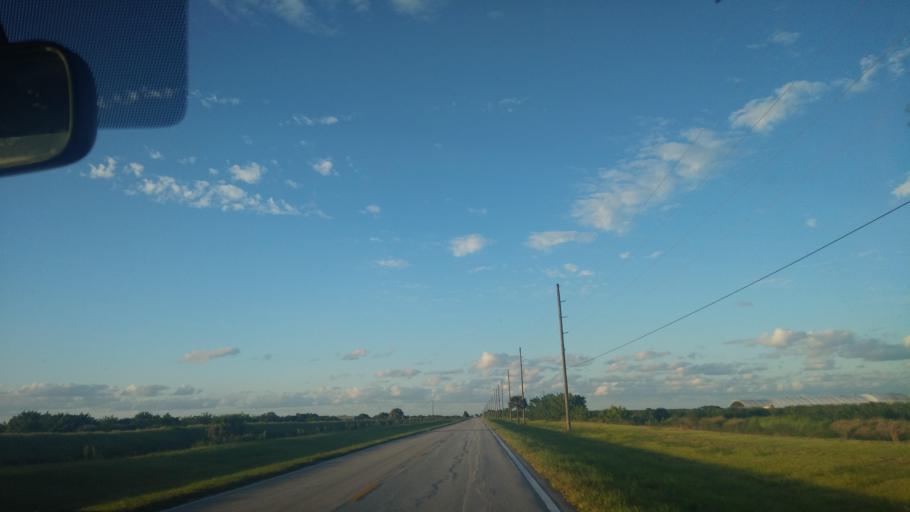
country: US
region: Florida
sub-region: Indian River County
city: Fellsmere
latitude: 27.7188
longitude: -80.6428
